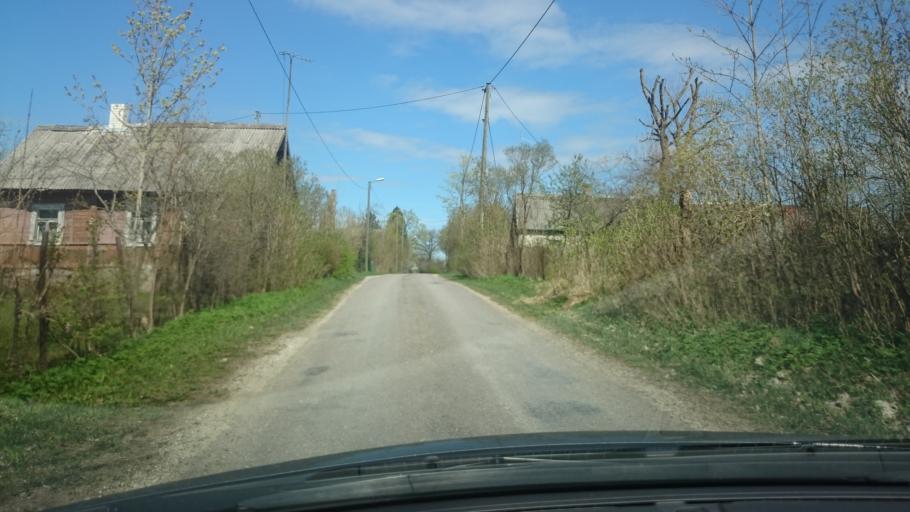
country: EE
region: Ida-Virumaa
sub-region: Sillamaee linn
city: Sillamae
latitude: 59.1191
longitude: 27.7995
